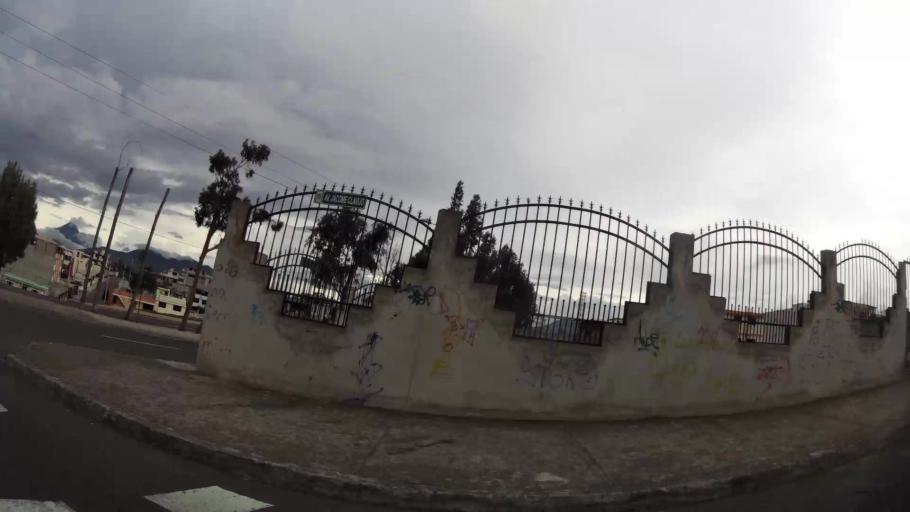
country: EC
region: Tungurahua
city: Ambato
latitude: -1.2748
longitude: -78.6257
